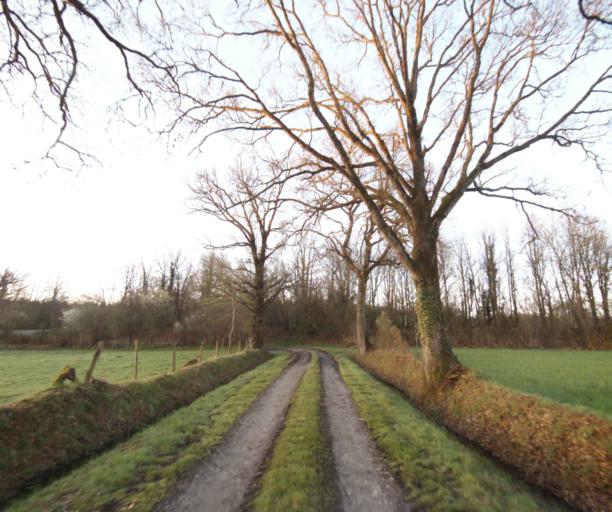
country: FR
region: Pays de la Loire
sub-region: Departement de la Loire-Atlantique
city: Campbon
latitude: 47.4191
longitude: -1.9100
